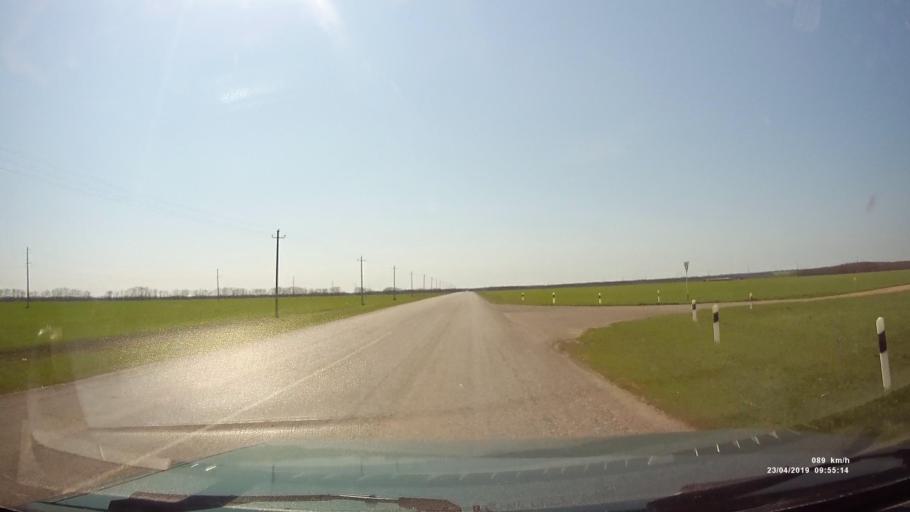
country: RU
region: Rostov
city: Orlovskiy
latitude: 46.8116
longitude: 42.0611
